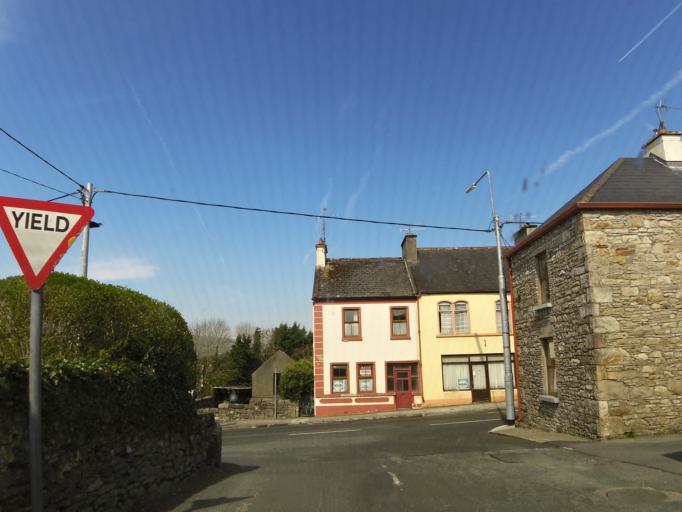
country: IE
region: Connaught
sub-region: Maigh Eo
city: Kiltamagh
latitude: 53.8471
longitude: -9.0028
